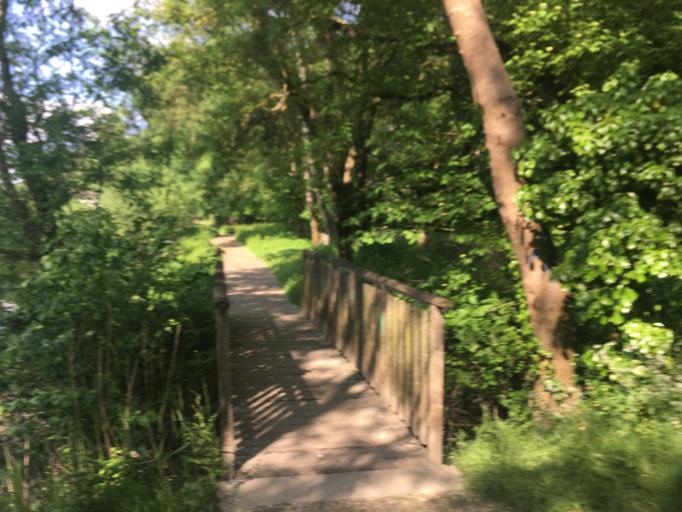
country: FR
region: Poitou-Charentes
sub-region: Departement de la Charente
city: Cognac
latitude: 45.6881
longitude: -0.3401
